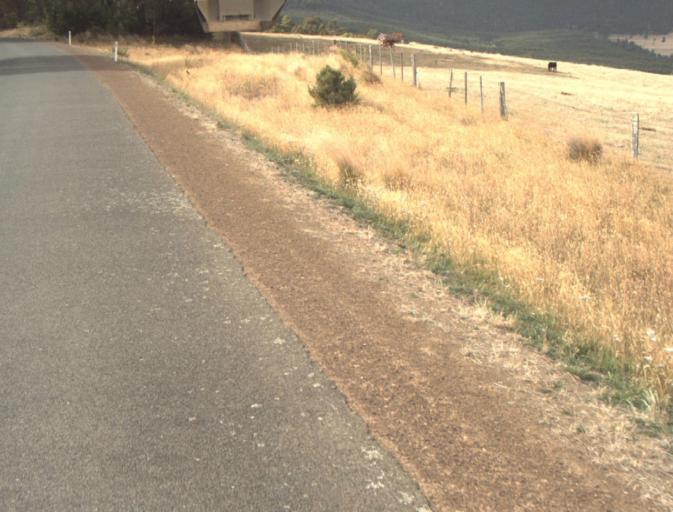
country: AU
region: Tasmania
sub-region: Dorset
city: Scottsdale
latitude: -41.4532
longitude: 147.5943
